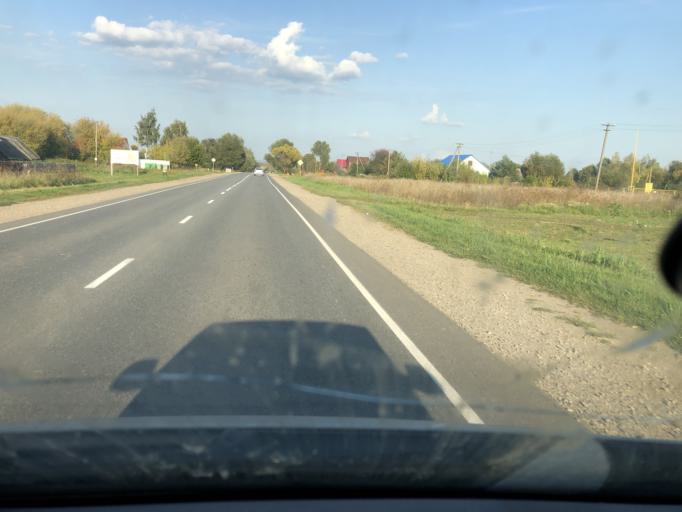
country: RU
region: Kaluga
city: Sosenskiy
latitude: 54.2110
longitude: 35.9845
